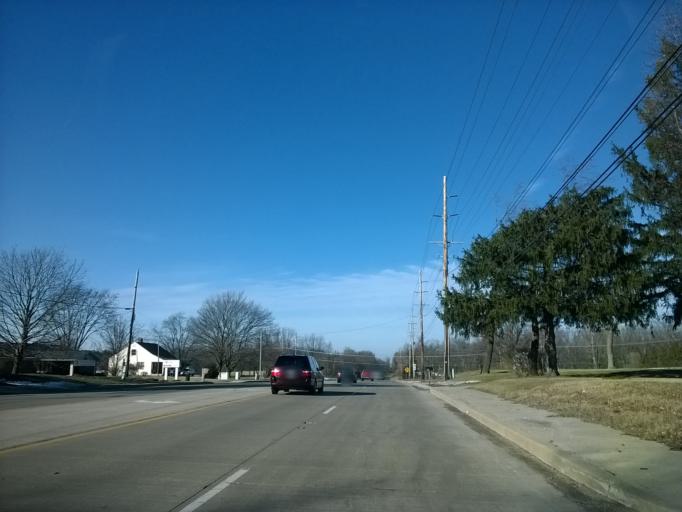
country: US
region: Indiana
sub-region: Boone County
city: Zionsville
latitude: 39.9605
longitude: -86.2462
